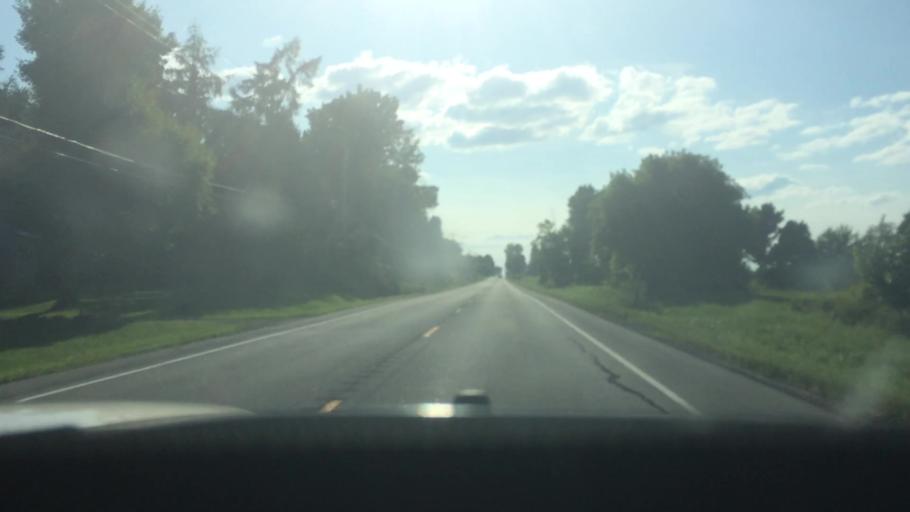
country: US
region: New York
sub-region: St. Lawrence County
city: Hannawa Falls
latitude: 44.6921
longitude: -74.6807
